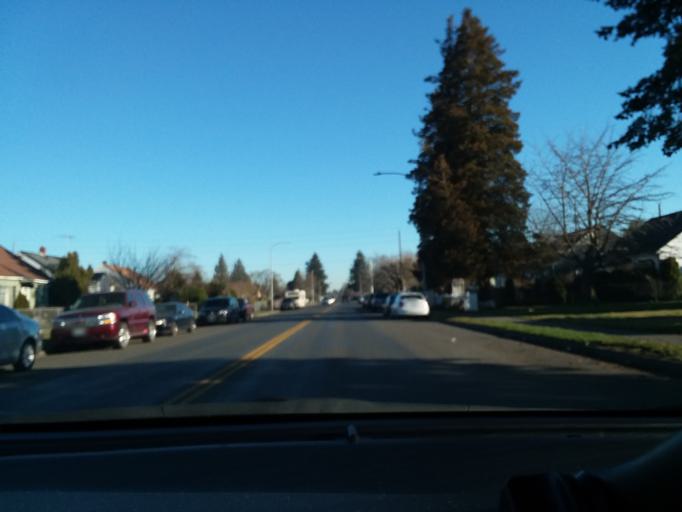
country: US
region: Washington
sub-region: Pierce County
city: Lakewood
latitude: 47.1940
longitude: -122.4724
